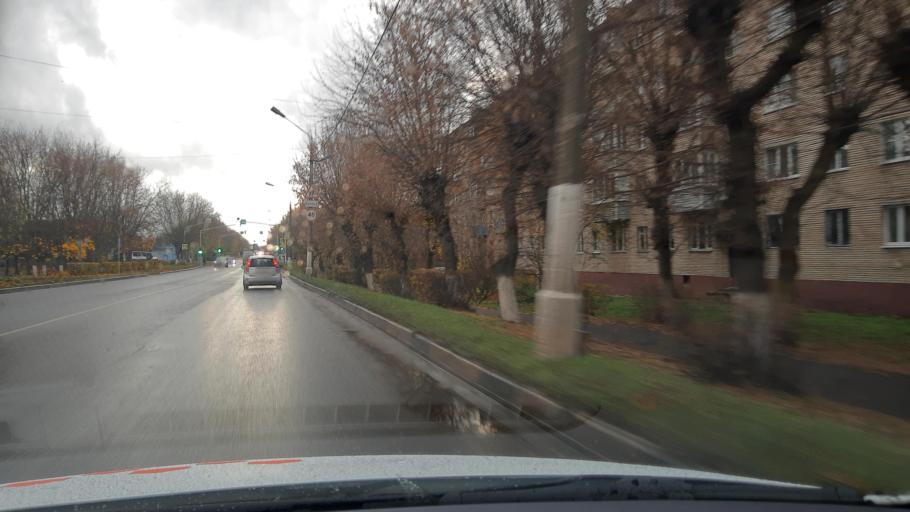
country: RU
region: Moskovskaya
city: Noginsk
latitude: 55.8408
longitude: 38.3993
